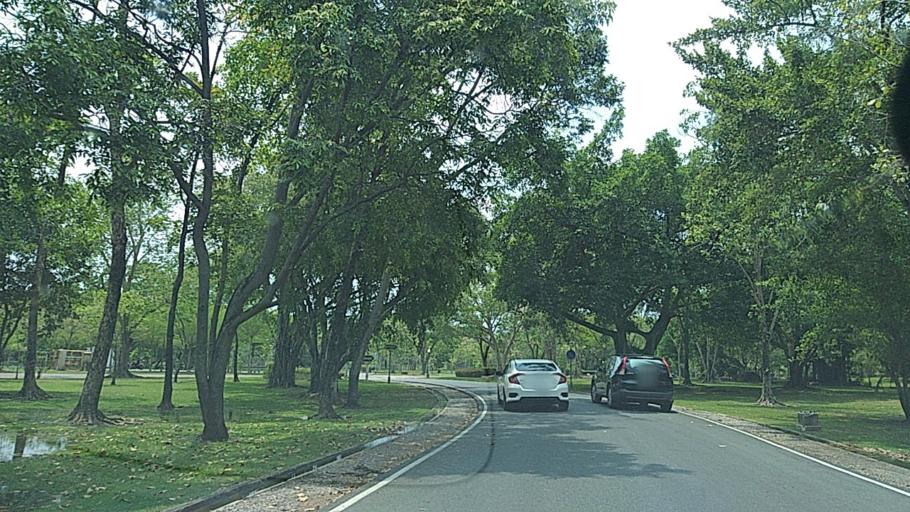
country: TH
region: Bangkok
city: Thawi Watthana
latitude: 13.7738
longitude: 100.3219
